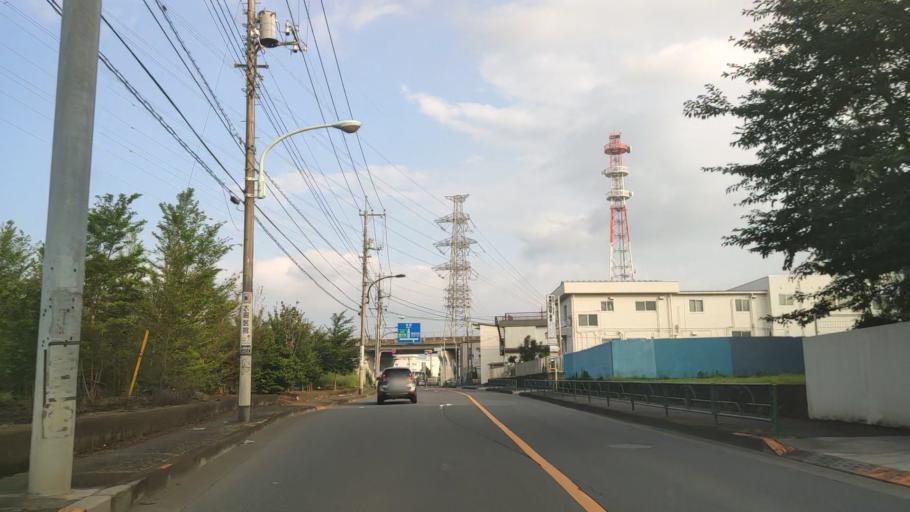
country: JP
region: Saitama
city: Hanno
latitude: 35.7968
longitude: 139.3167
